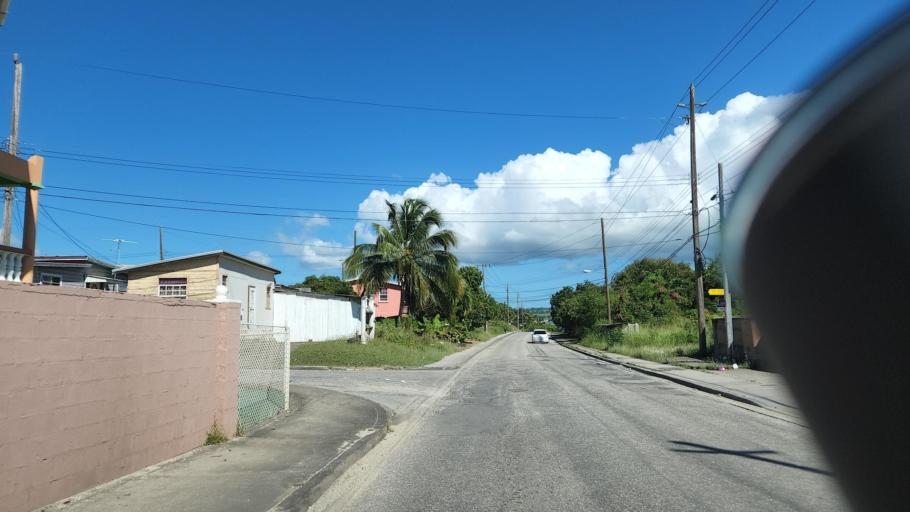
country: BB
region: Saint Thomas
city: Welchman Hall
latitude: 13.1485
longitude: -59.5973
